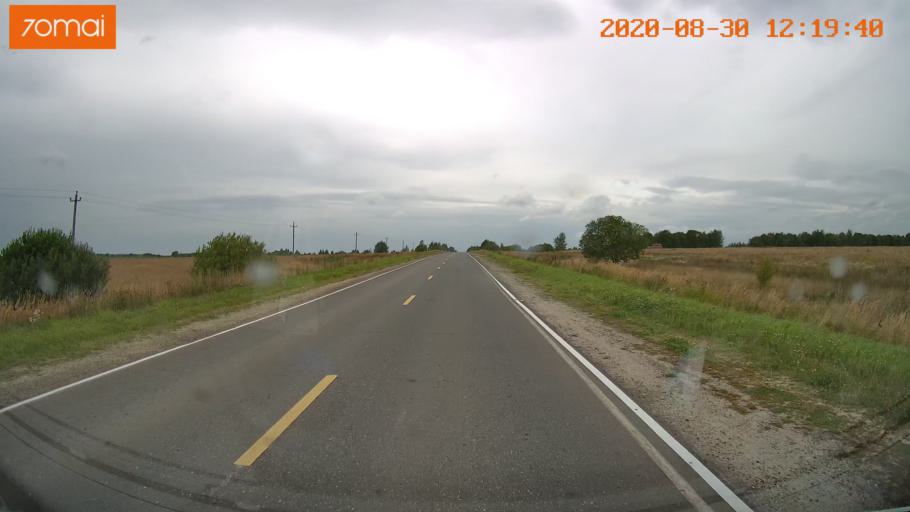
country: RU
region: Ivanovo
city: Yur'yevets
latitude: 57.3230
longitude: 42.9217
